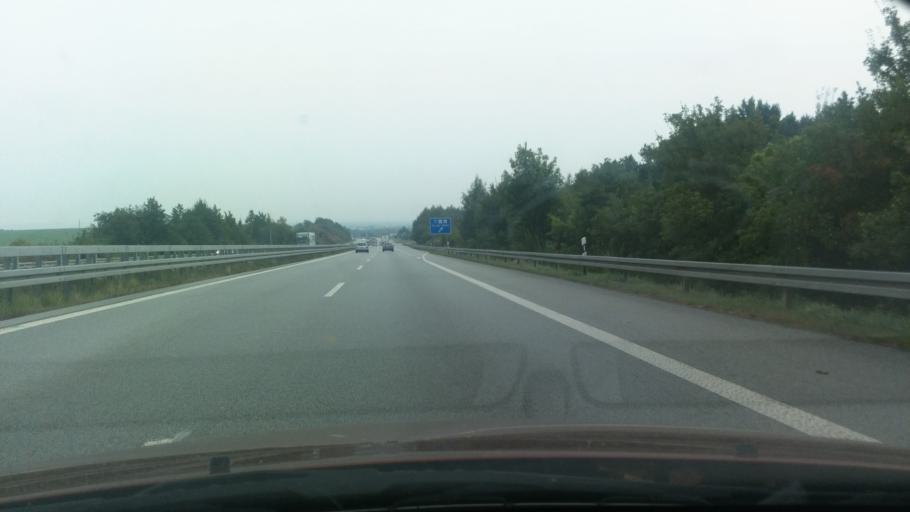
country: DE
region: Saxony
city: Goerlitz
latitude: 51.1912
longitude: 14.9782
